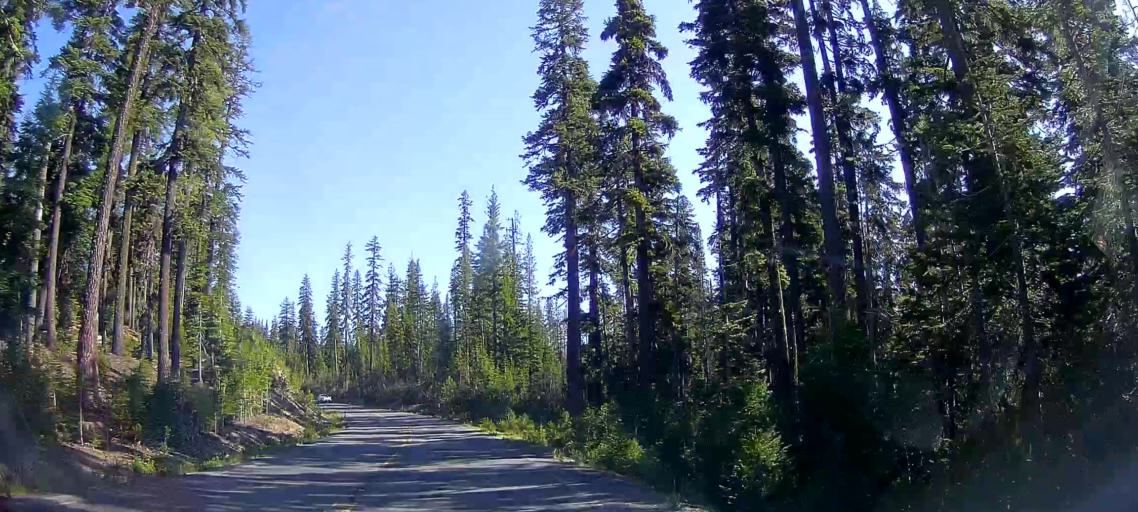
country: US
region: Oregon
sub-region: Jackson County
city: Shady Cove
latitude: 42.8467
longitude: -122.1464
